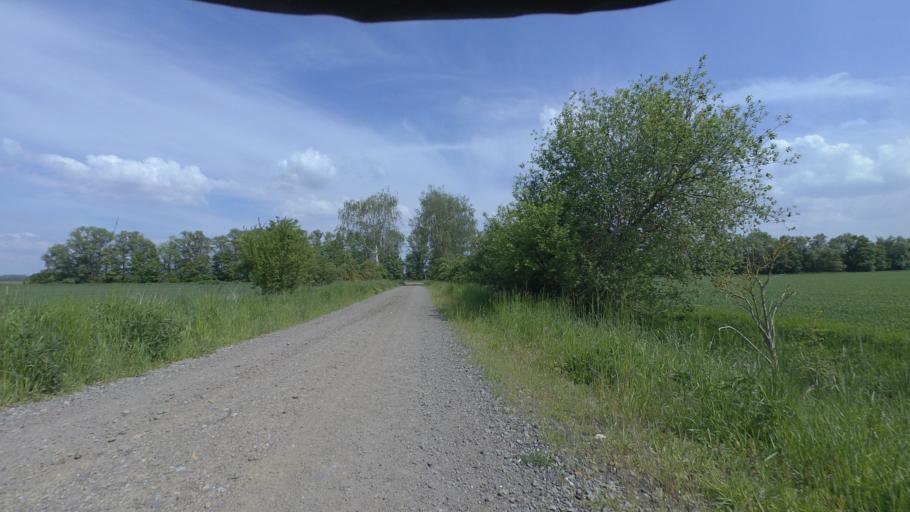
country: DE
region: Lower Saxony
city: Sollingen
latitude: 52.0655
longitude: 10.9428
